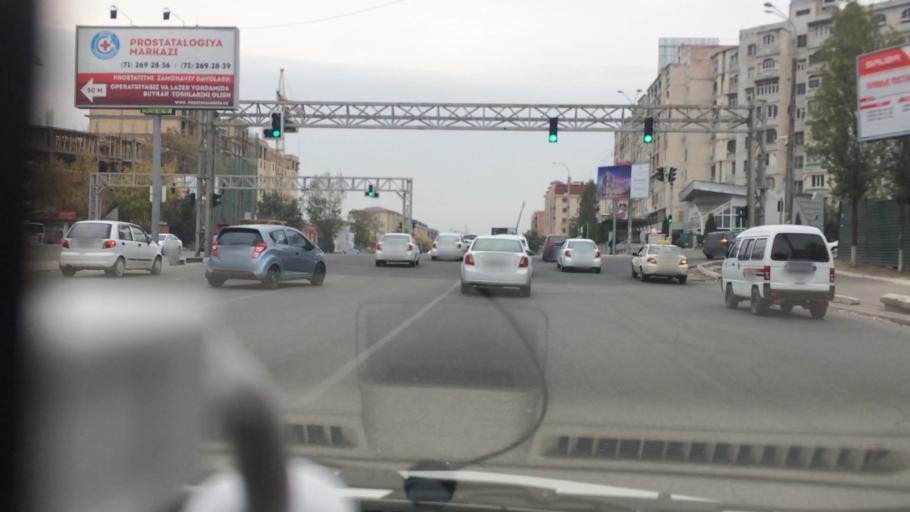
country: UZ
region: Toshkent
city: Salor
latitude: 41.3132
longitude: 69.3306
